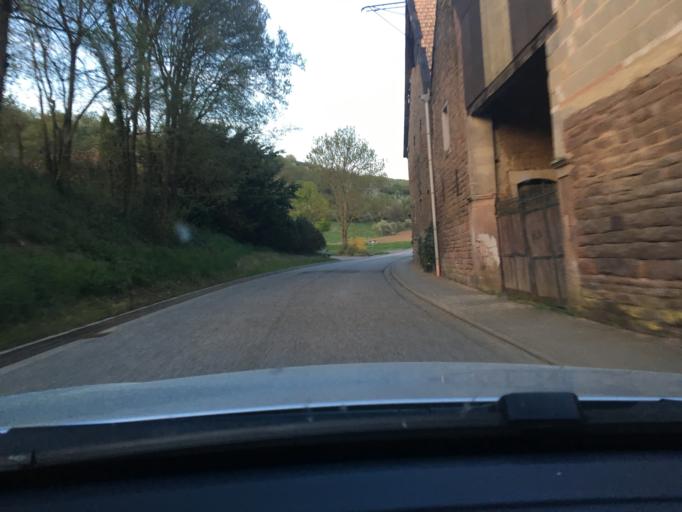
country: DE
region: Rheinland-Pfalz
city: Oberhausen an der Appel
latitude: 49.7149
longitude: 7.8847
